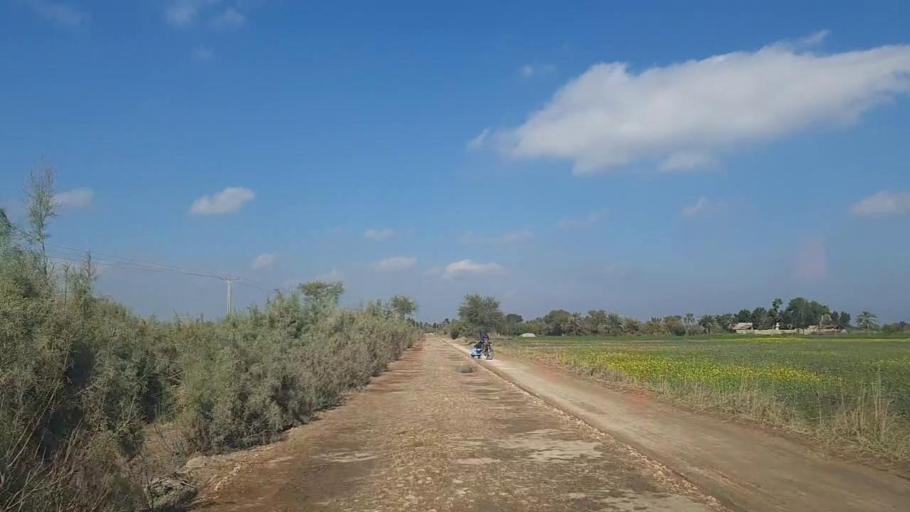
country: PK
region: Sindh
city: Sanghar
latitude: 26.0767
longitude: 68.9865
